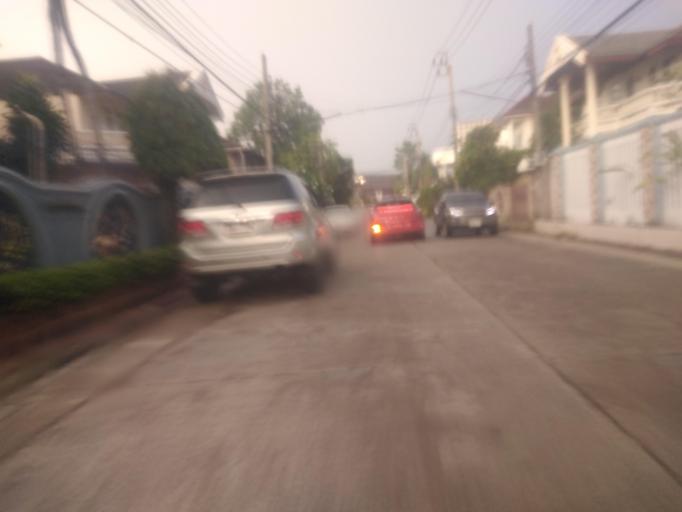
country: TH
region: Bangkok
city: Phasi Charoen
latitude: 13.7420
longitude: 100.4448
